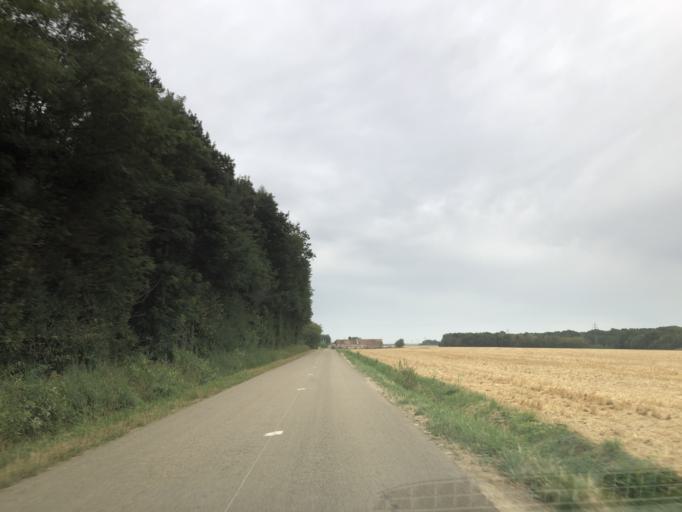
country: FR
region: Centre
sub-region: Departement du Loiret
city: Courtenay
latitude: 47.9907
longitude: 3.1430
